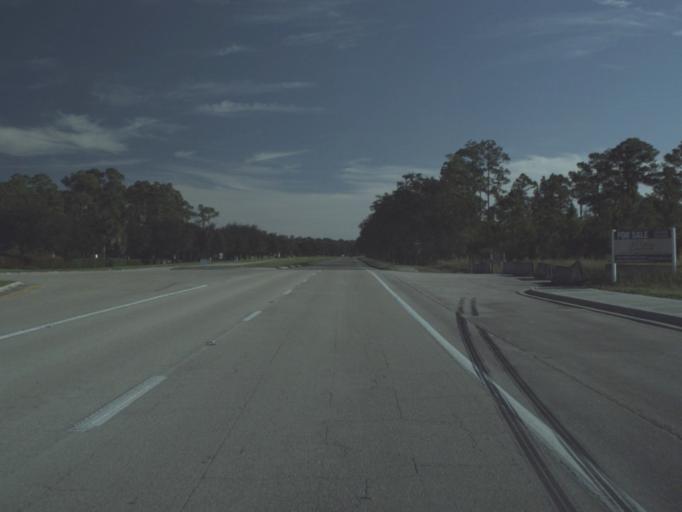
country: US
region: Florida
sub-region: Lee County
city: Palmona Park
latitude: 26.7165
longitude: -81.9216
